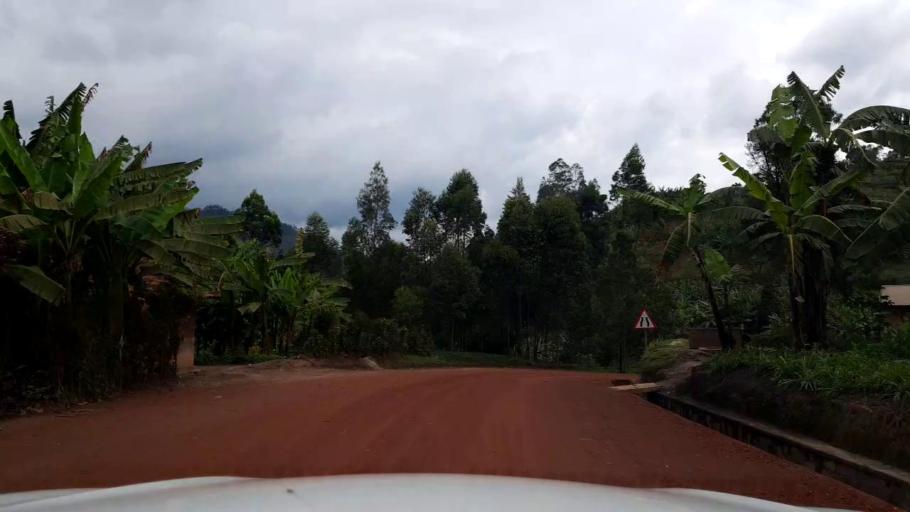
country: RW
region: Northern Province
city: Musanze
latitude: -1.6667
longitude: 29.8014
